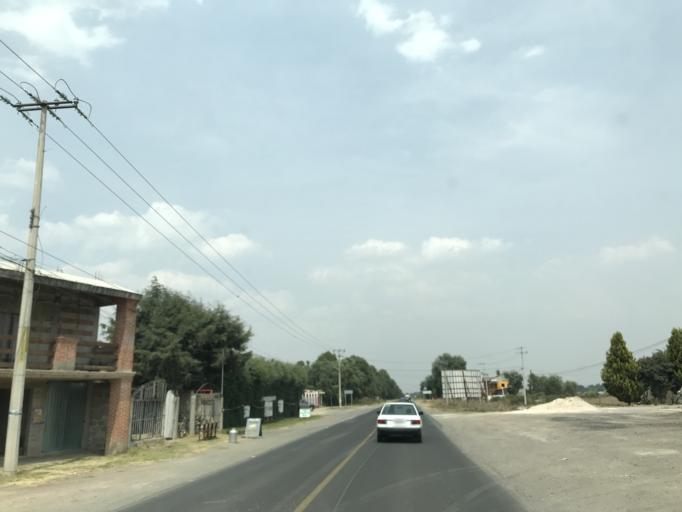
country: MX
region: Tlaxcala
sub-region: Ixtacuixtla de Mariano Matamoros
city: Santa Justina Ecatepec
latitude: 19.3079
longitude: -98.3693
